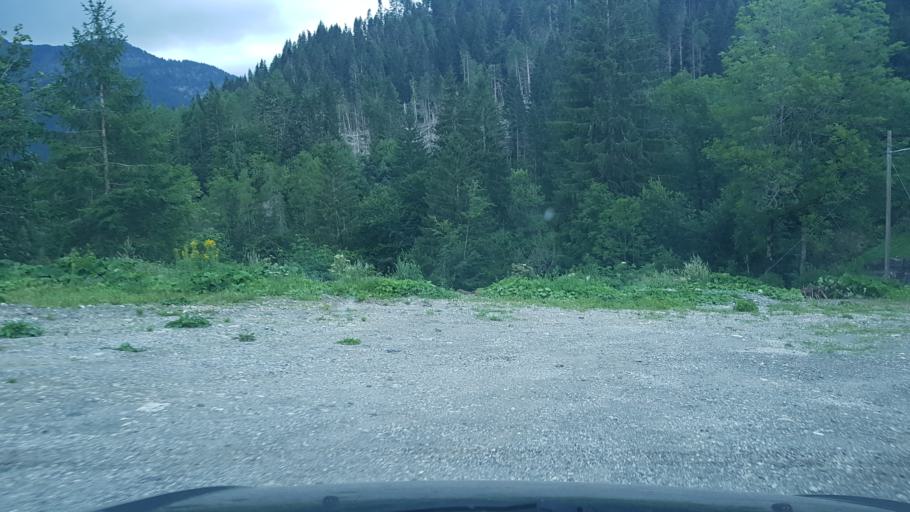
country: IT
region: Friuli Venezia Giulia
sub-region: Provincia di Udine
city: Forni Avoltri
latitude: 46.5812
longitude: 12.7963
